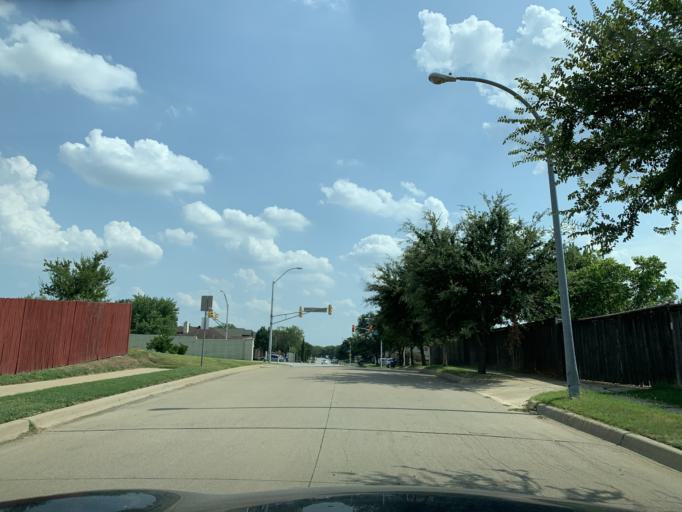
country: US
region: Texas
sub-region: Tarrant County
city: Hurst
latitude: 32.8034
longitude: -97.1949
